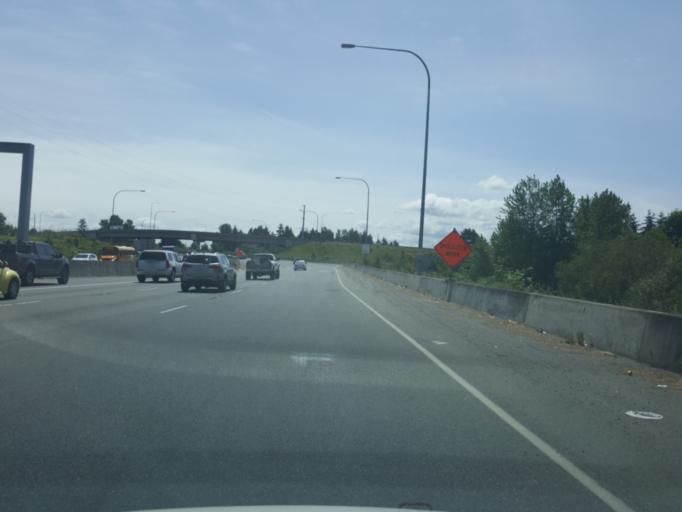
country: US
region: Washington
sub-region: Pierce County
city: Fircrest
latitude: 47.2382
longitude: -122.5011
